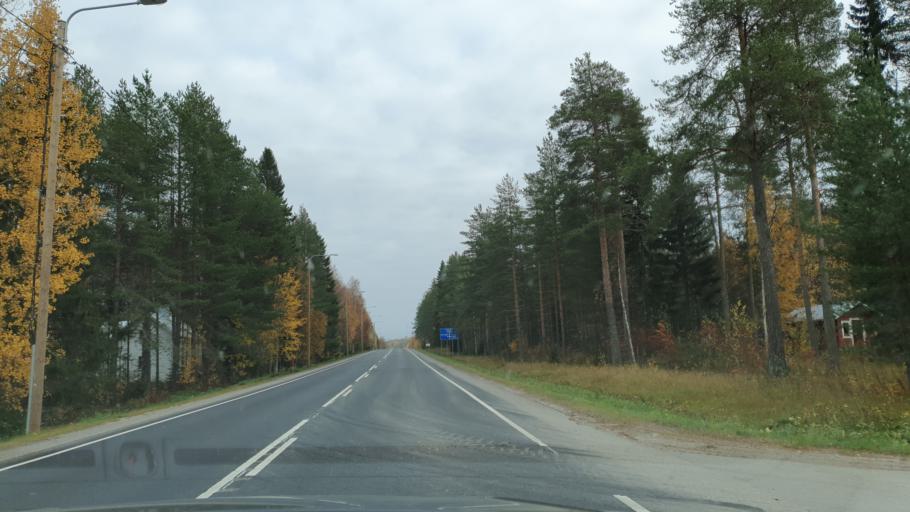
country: FI
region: Kainuu
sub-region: Kajaani
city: Ristijaervi
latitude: 64.4978
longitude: 28.2088
